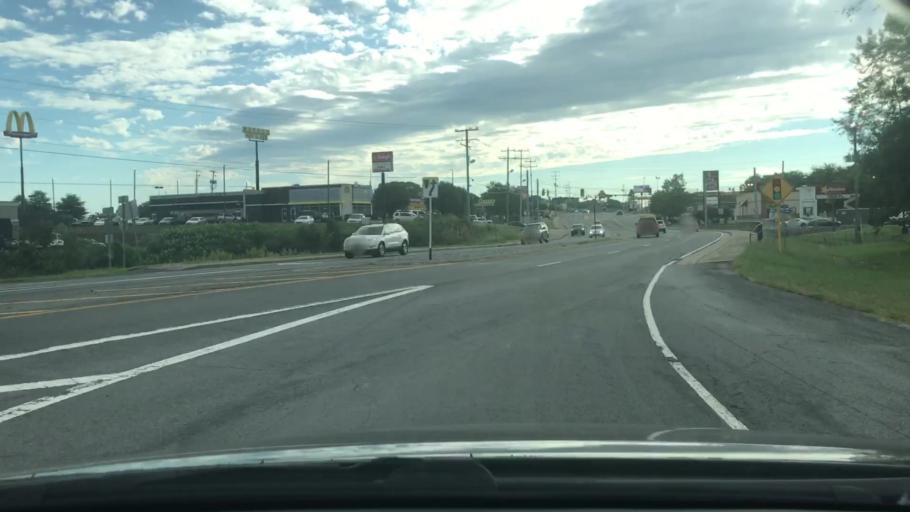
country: US
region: Tennessee
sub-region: Sumner County
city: White House
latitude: 36.4689
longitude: -86.6796
